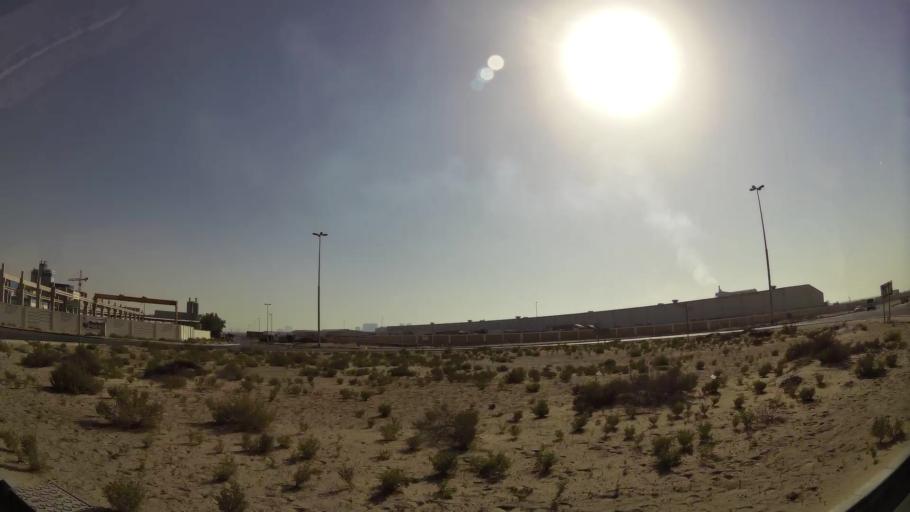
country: AE
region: Dubai
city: Dubai
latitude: 24.9954
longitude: 55.1259
